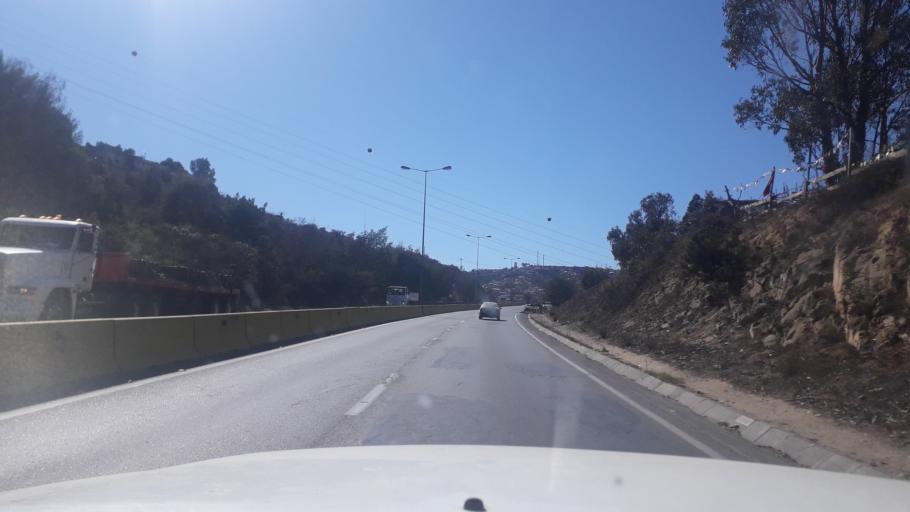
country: CL
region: Valparaiso
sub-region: Provincia de Valparaiso
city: Vina del Mar
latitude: -33.0319
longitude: -71.5005
